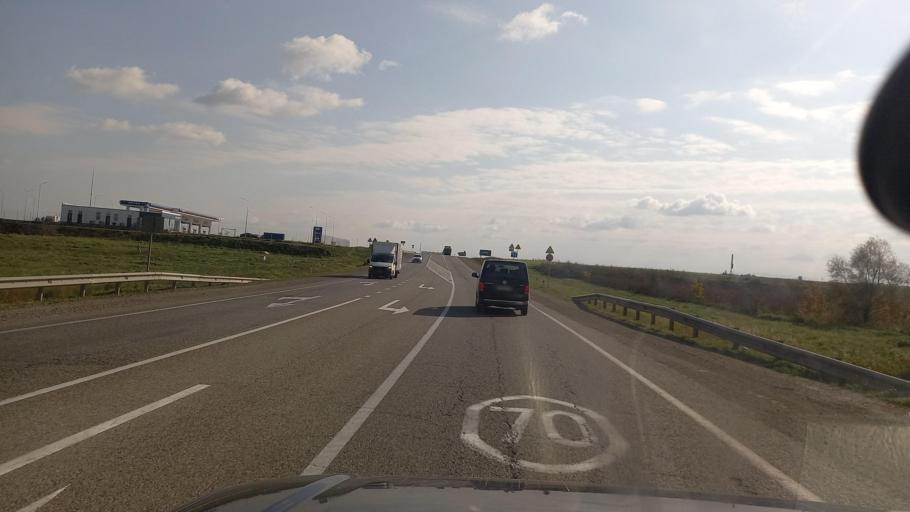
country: RU
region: Krasnodarskiy
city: Abinsk
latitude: 44.8745
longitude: 38.1122
